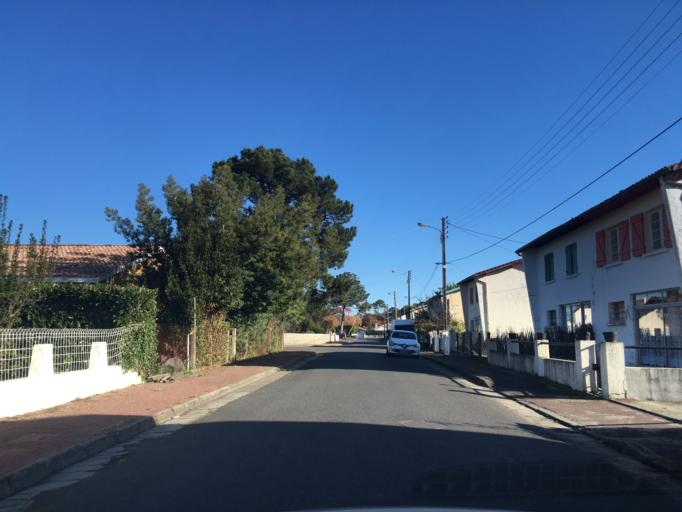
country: FR
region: Aquitaine
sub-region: Departement de la Gironde
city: La Teste-de-Buch
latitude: 44.6174
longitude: -1.1411
